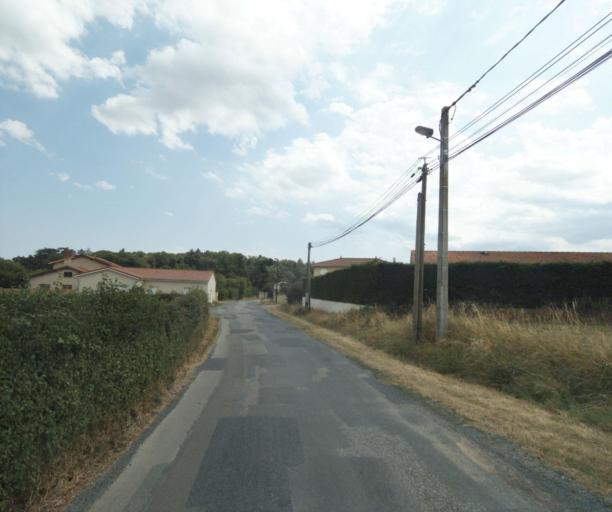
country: FR
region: Rhone-Alpes
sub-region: Departement du Rhone
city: Bully
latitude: 45.8601
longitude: 4.5777
